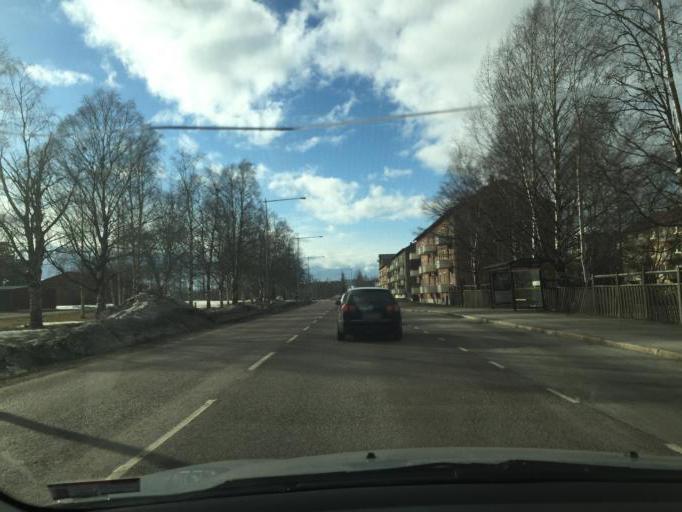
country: SE
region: Norrbotten
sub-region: Lulea Kommun
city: Lulea
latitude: 65.5795
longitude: 22.1804
